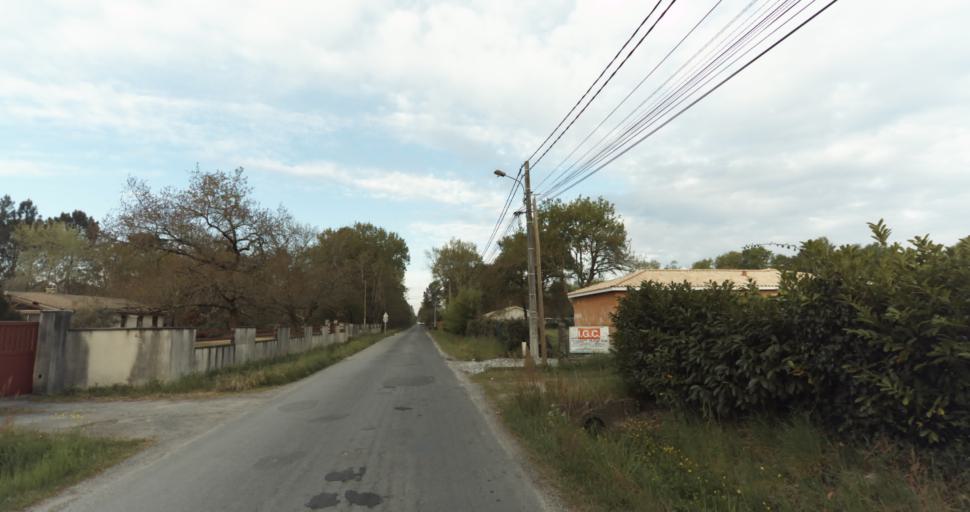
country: FR
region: Aquitaine
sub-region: Departement de la Gironde
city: Saint-Aubin-de-Medoc
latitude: 44.7732
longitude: -0.7387
